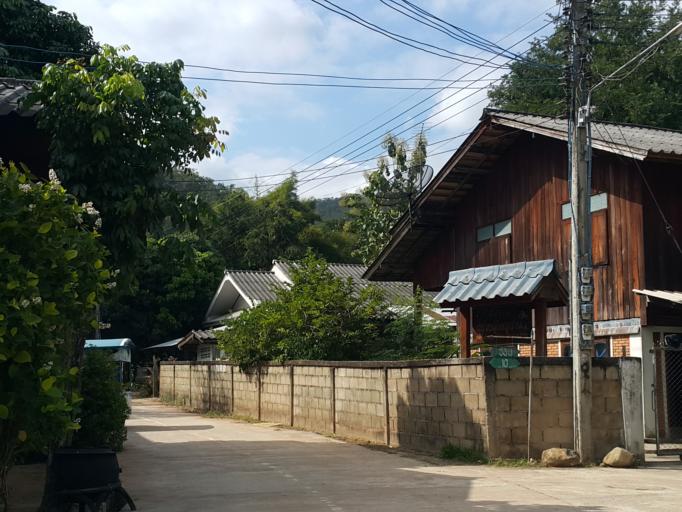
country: TH
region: Lampang
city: Chae Hom
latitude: 18.5625
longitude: 99.4482
